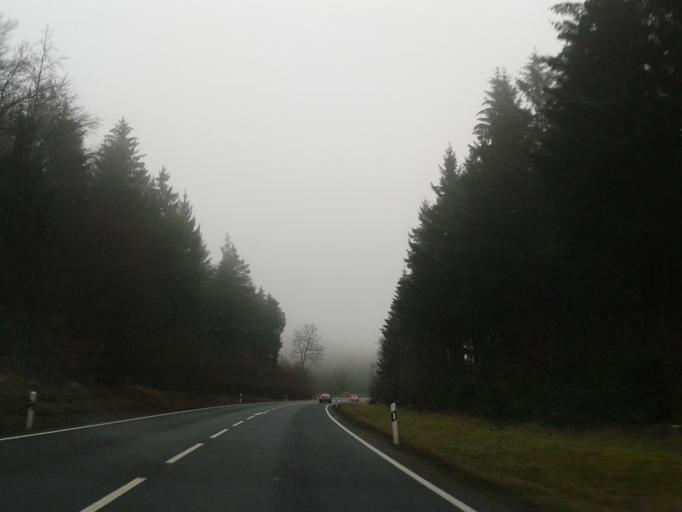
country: DE
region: Bavaria
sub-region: Regierungsbezirk Unterfranken
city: Burgpreppach
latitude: 50.1358
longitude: 10.5928
